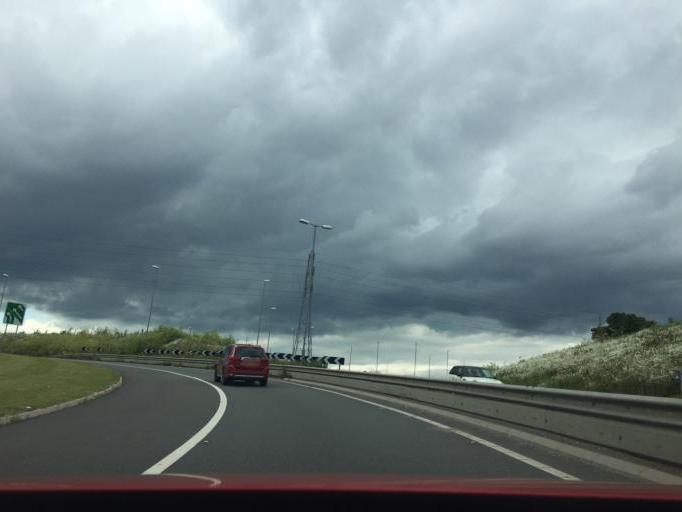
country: GB
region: England
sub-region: Luton
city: Luton
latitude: 51.8575
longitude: -0.4150
